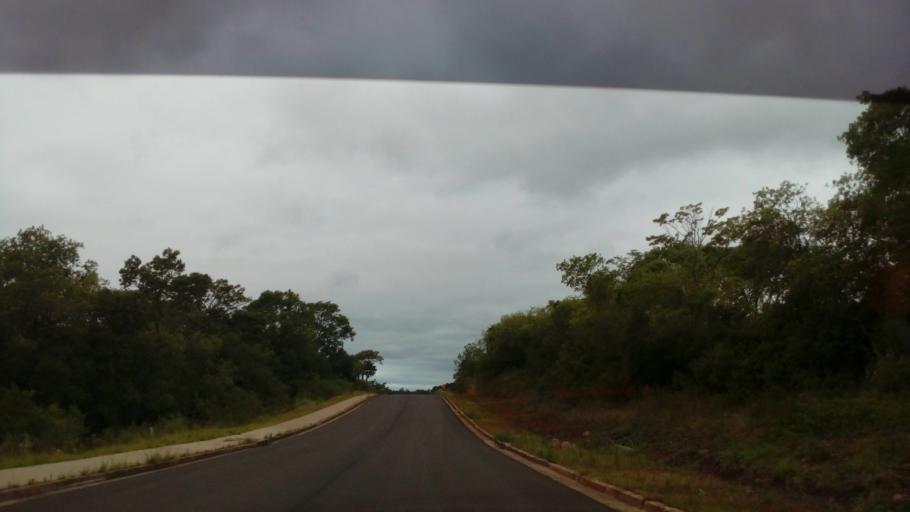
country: AR
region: Misiones
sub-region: Departamento de Candelaria
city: Candelaria
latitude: -27.4501
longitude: -55.7696
